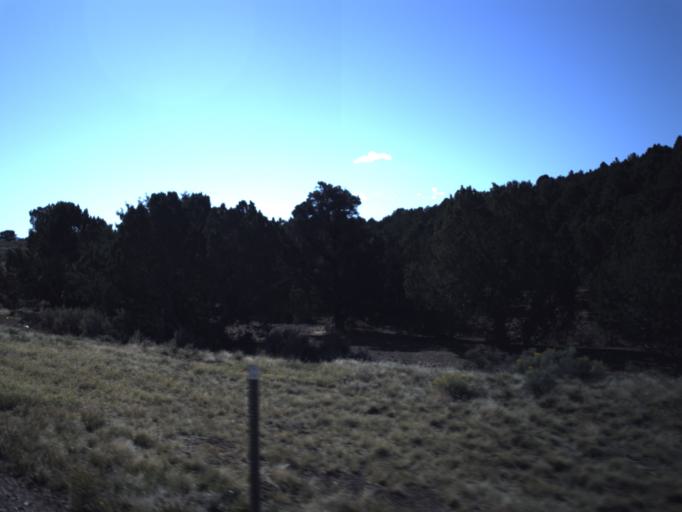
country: US
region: Utah
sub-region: Washington County
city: Enterprise
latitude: 37.6730
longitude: -113.4897
